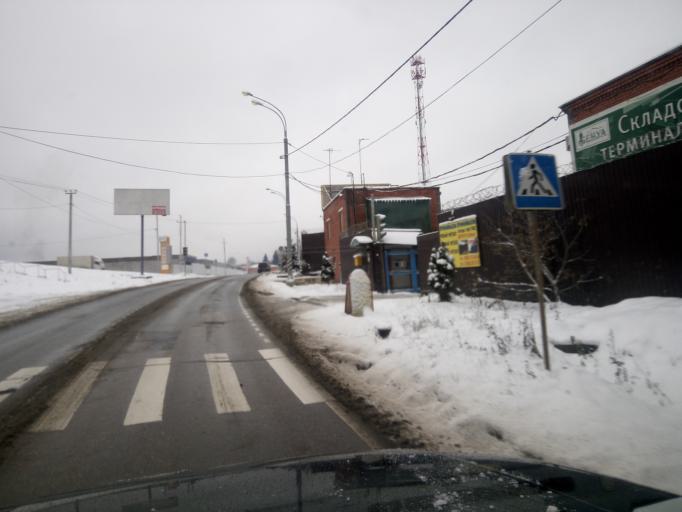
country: RU
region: Moskovskaya
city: Skhodnya
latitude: 55.9696
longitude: 37.3100
